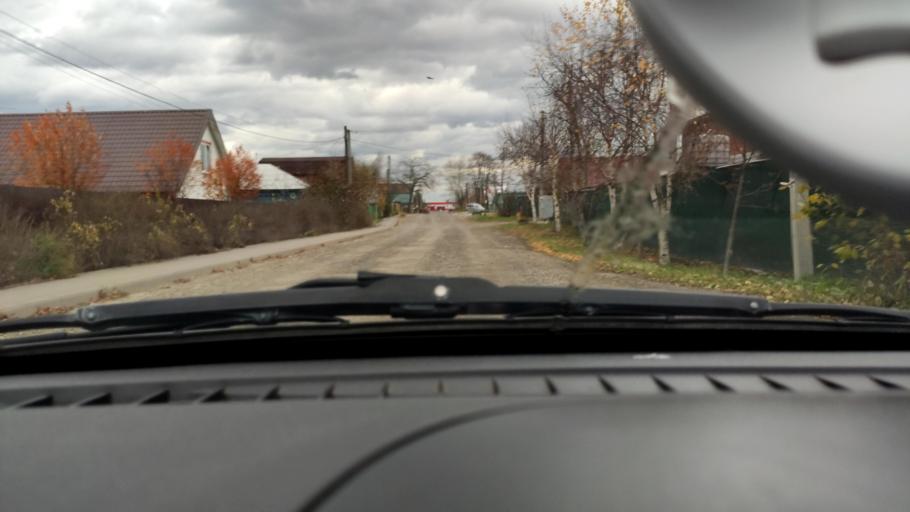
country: RU
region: Perm
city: Kondratovo
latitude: 57.9819
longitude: 56.0991
